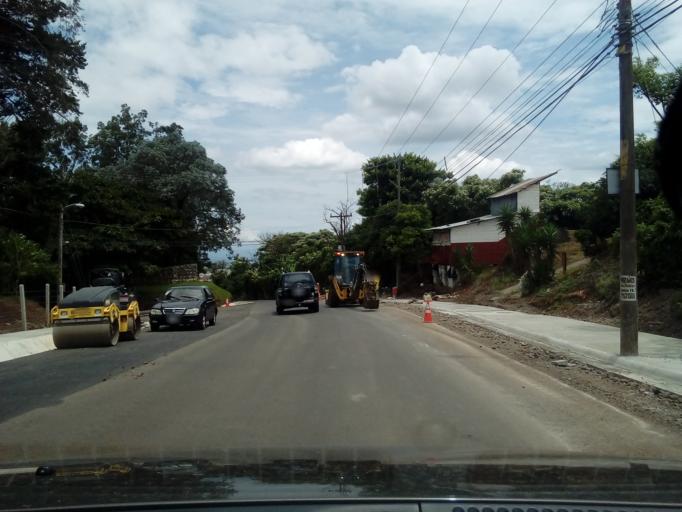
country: CR
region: Heredia
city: San Josecito
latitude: 10.0215
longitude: -84.0844
